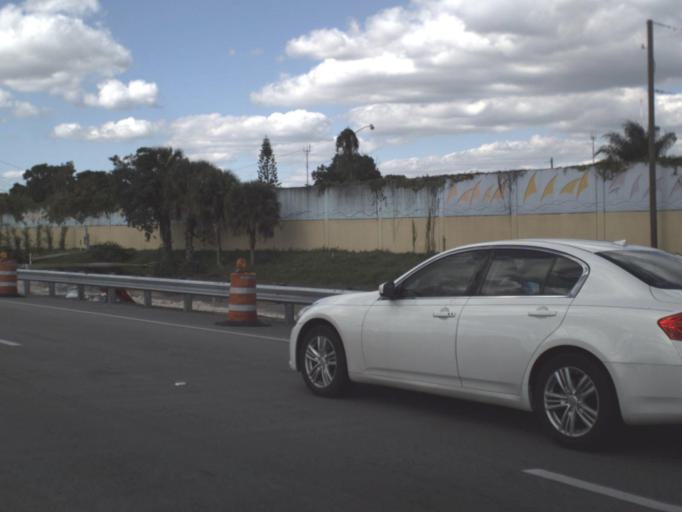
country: US
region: Florida
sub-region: Miami-Dade County
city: Norland
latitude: 25.9361
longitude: -80.2168
